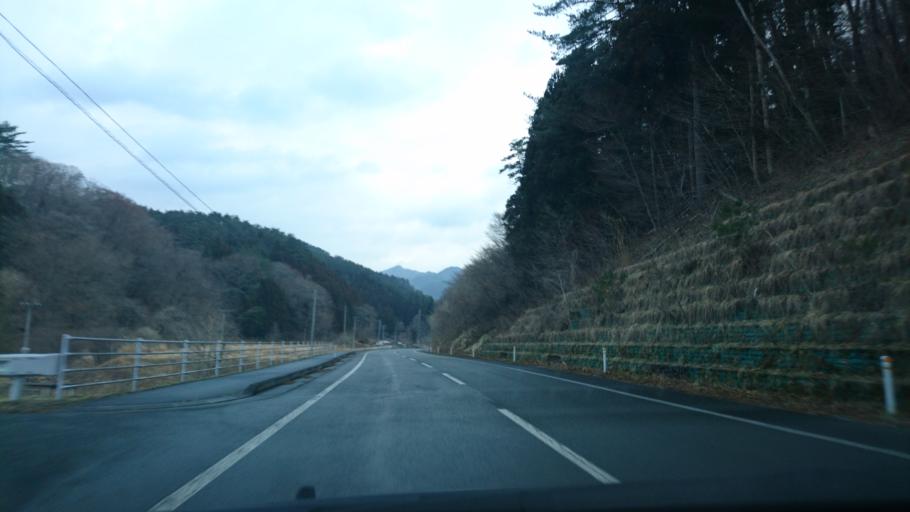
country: JP
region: Iwate
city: Ofunato
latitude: 39.0076
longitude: 141.5444
